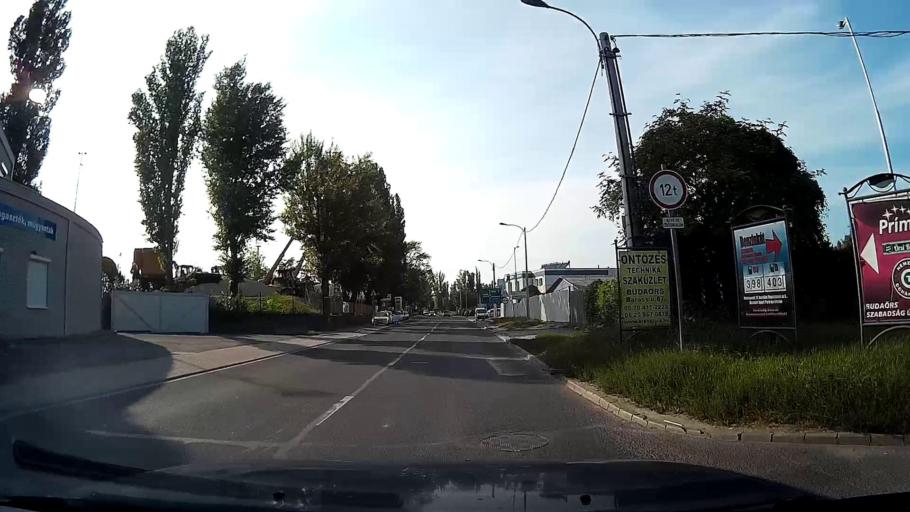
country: HU
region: Pest
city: Budaors
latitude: 47.4454
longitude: 18.9778
